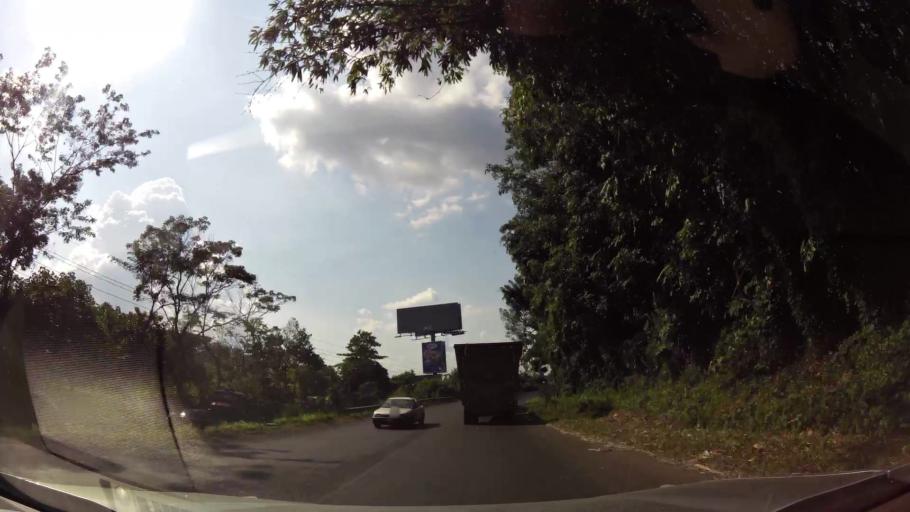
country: GT
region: Retalhuleu
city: San Sebastian
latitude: 14.5521
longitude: -91.6382
